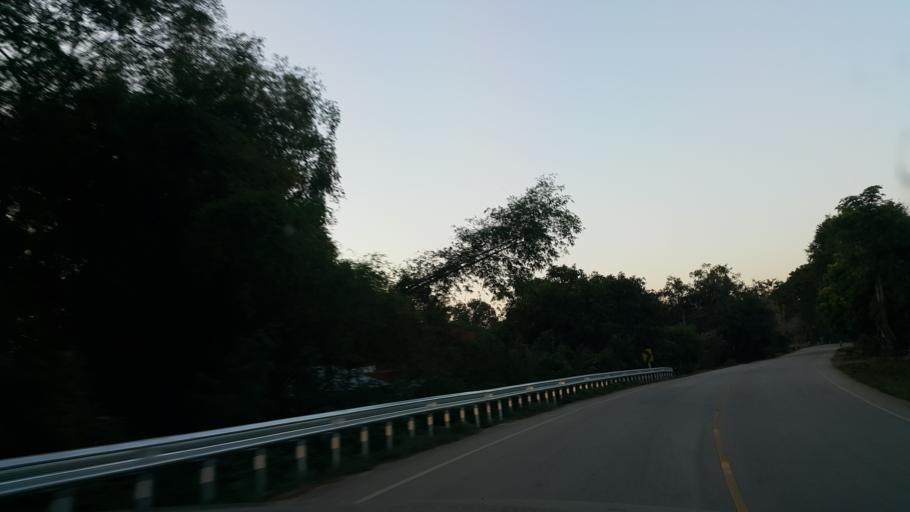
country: TH
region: Phrae
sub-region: Amphoe Wang Chin
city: Wang Chin
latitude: 17.8707
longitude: 99.6194
